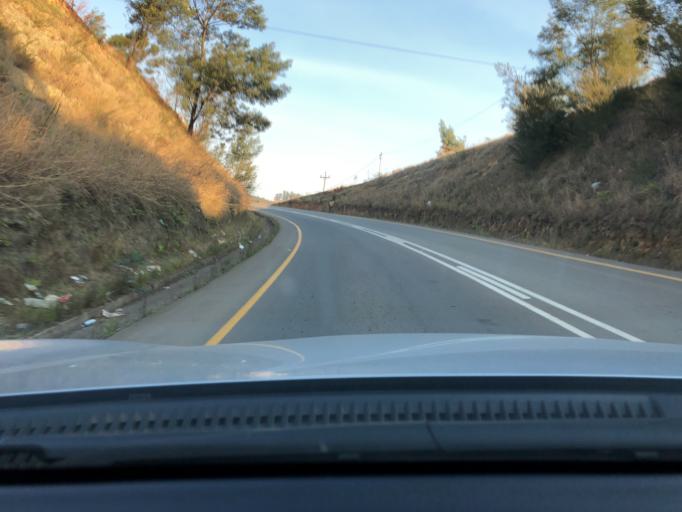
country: ZA
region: KwaZulu-Natal
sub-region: Sisonke District Municipality
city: Ixopo
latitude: -30.1629
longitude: 30.0596
